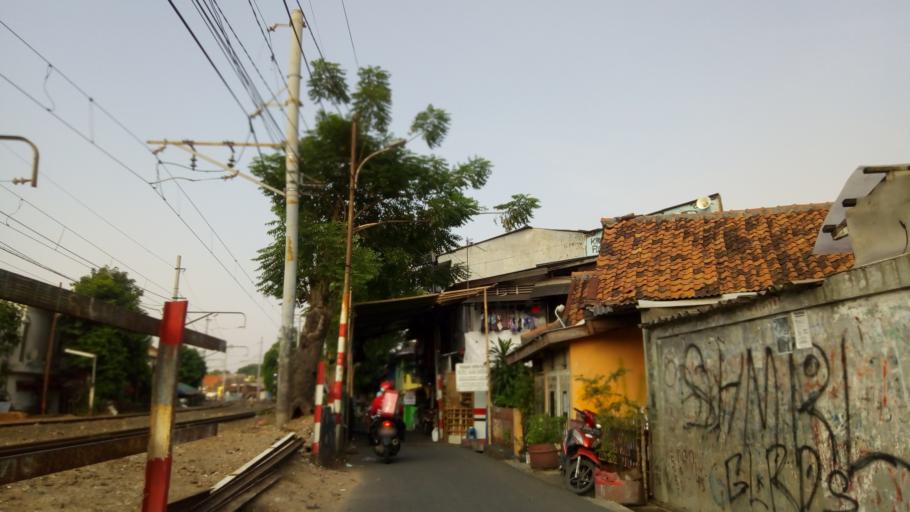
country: ID
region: Jakarta Raya
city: Jakarta
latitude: -6.2067
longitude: 106.8418
